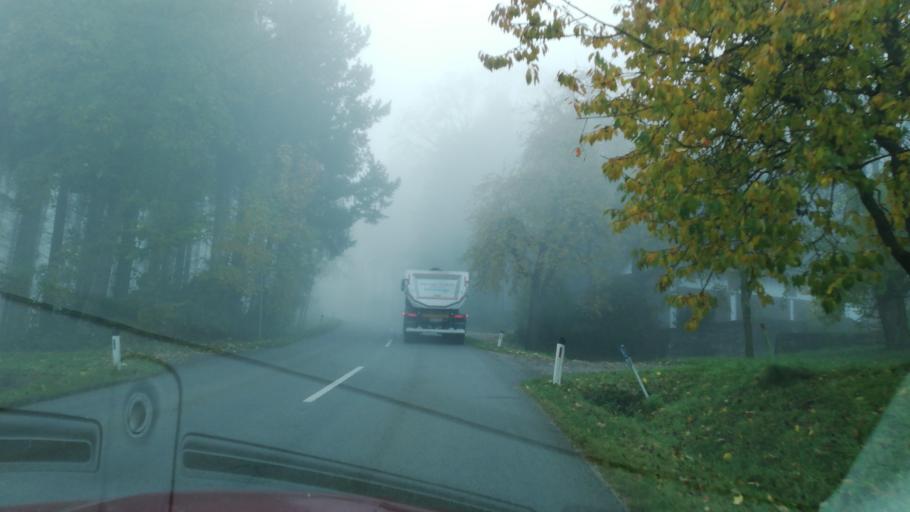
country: AT
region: Upper Austria
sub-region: Politischer Bezirk Grieskirchen
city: Bad Schallerbach
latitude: 48.1783
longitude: 13.9091
